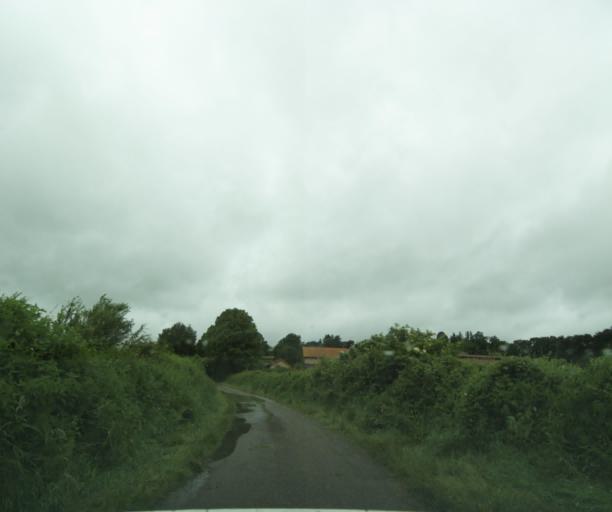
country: FR
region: Bourgogne
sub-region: Departement de Saone-et-Loire
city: Charolles
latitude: 46.5020
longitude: 4.3568
